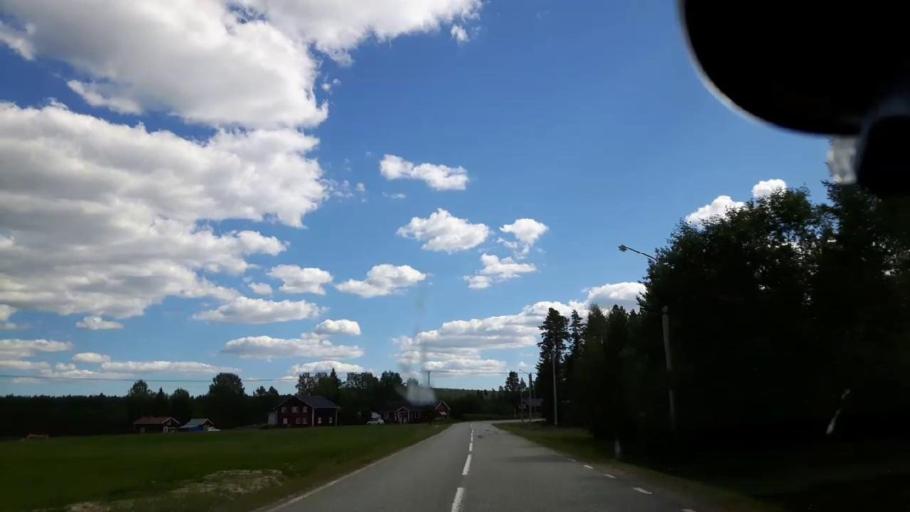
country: SE
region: Jaemtland
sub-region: Ragunda Kommun
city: Hammarstrand
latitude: 62.8905
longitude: 16.2239
